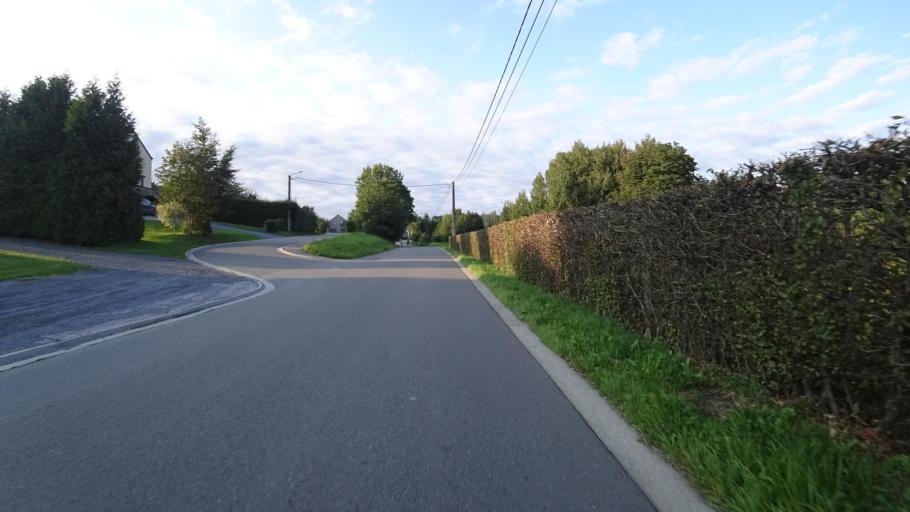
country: BE
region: Wallonia
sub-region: Province du Luxembourg
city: Neufchateau
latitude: 49.8995
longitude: 5.3858
